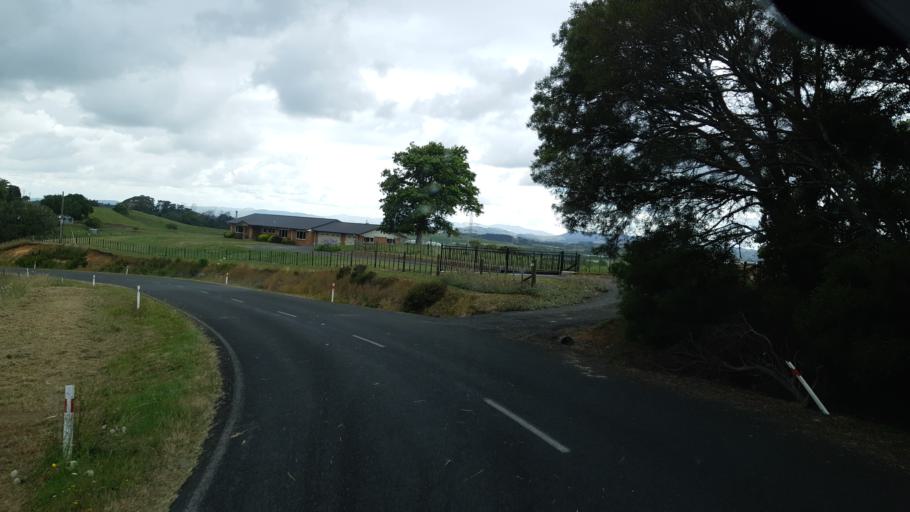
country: NZ
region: Waikato
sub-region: Waikato District
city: Ngaruawahia
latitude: -37.5497
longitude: 175.0734
